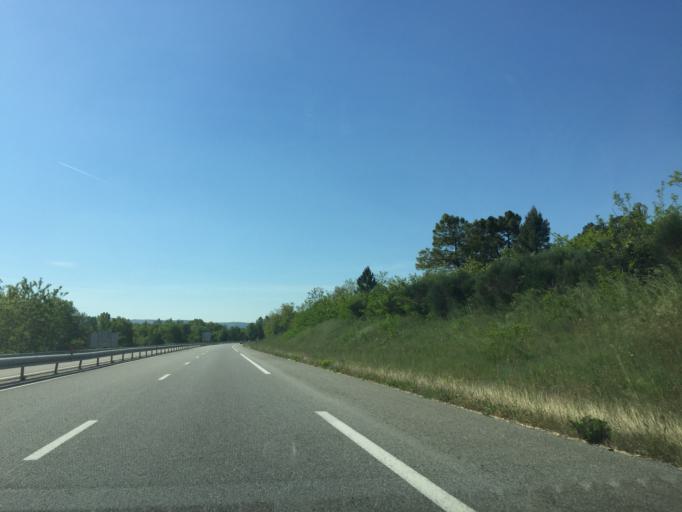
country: FR
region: Provence-Alpes-Cote d'Azur
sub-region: Departement des Alpes-de-Haute-Provence
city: Oraison
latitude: 43.9300
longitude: 5.8954
